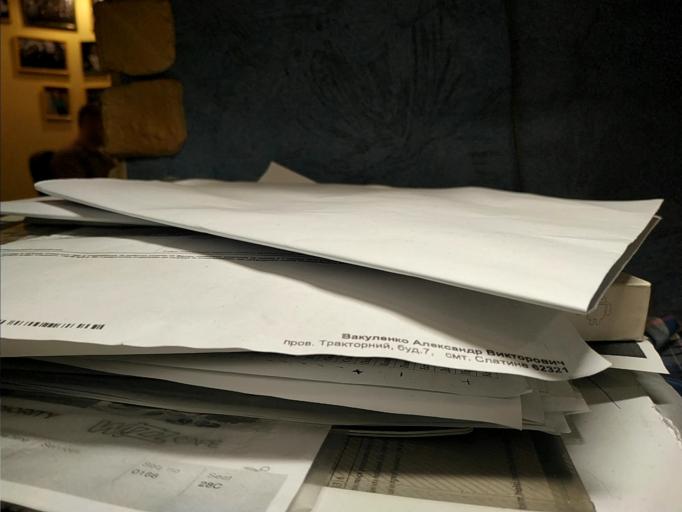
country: RU
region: Tverskaya
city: Zubtsov
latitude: 56.1303
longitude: 34.5152
